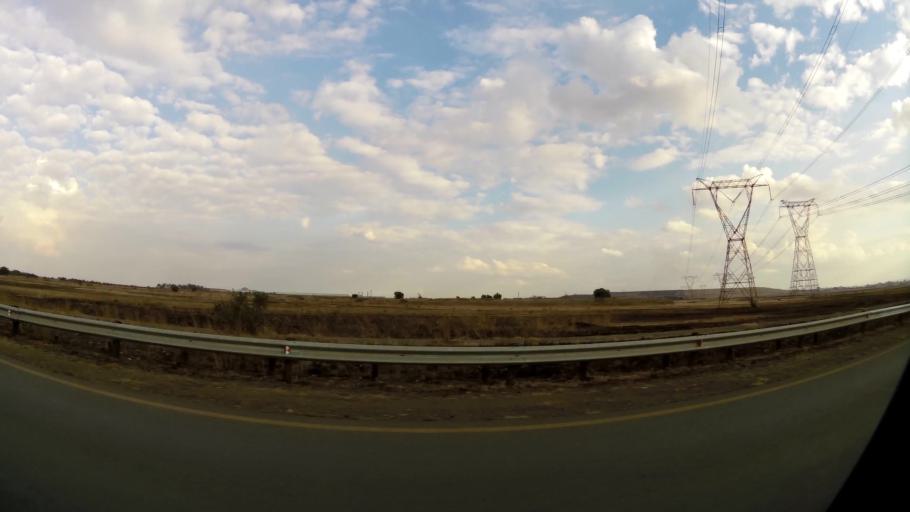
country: ZA
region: Gauteng
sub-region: Sedibeng District Municipality
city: Vanderbijlpark
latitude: -26.6191
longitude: 27.8289
